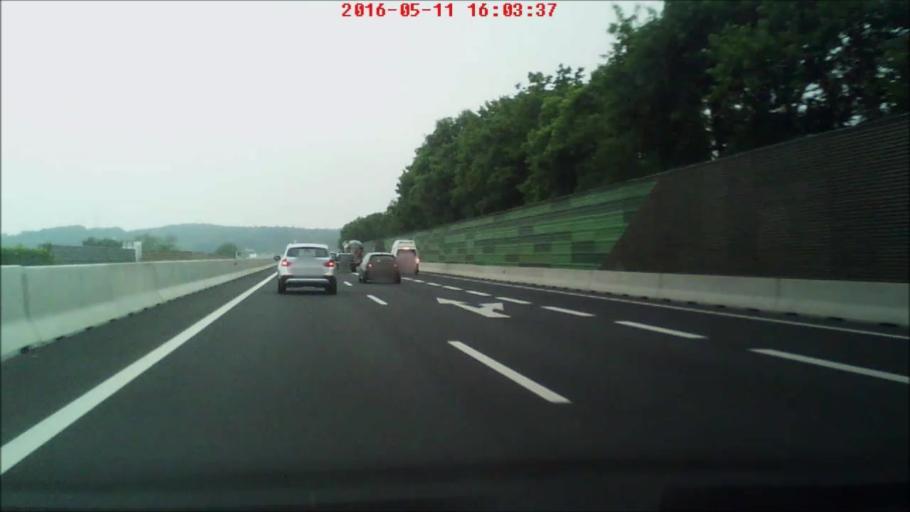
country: AT
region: Styria
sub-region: Politischer Bezirk Leibnitz
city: Weitendorf
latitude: 46.8972
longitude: 15.4721
